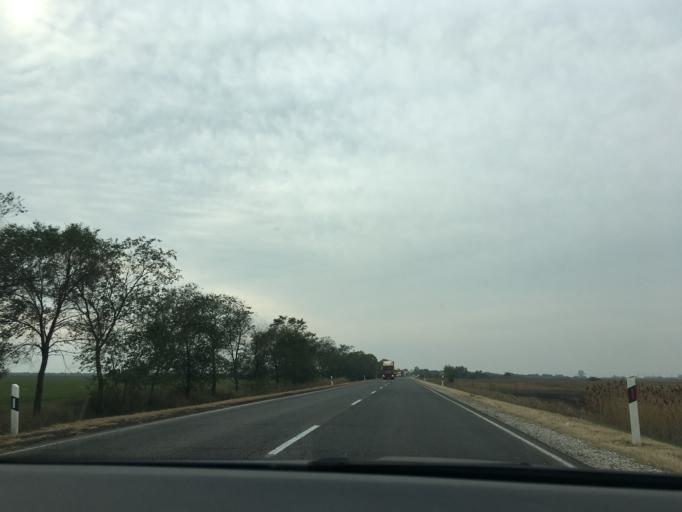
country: HU
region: Jasz-Nagykun-Szolnok
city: Karcag
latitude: 47.2766
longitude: 20.8885
